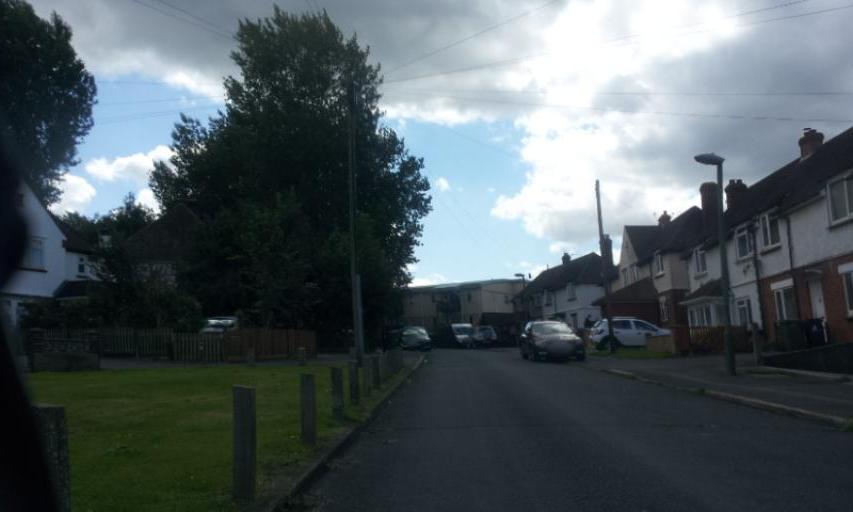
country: GB
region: England
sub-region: Kent
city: Maidstone
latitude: 51.2625
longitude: 0.5361
